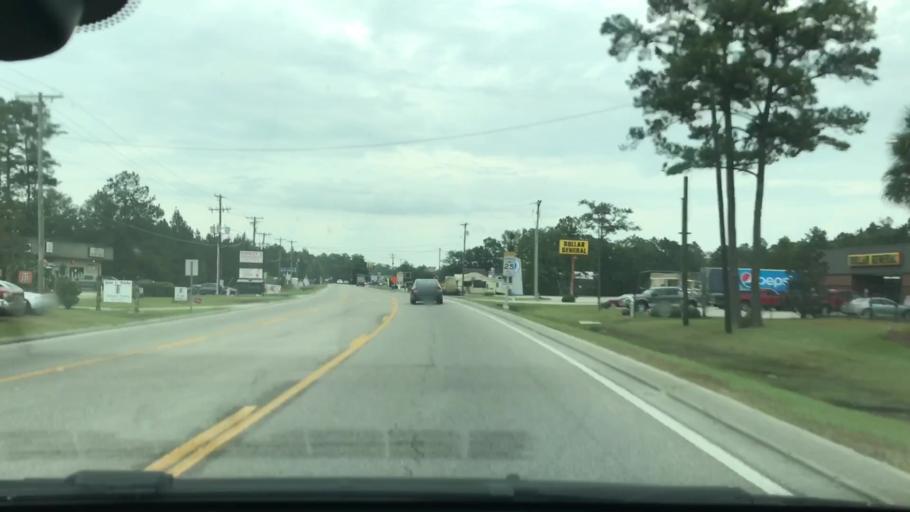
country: US
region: Louisiana
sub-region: Saint Tammany Parish
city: Pearl River
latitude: 30.3639
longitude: -89.7558
